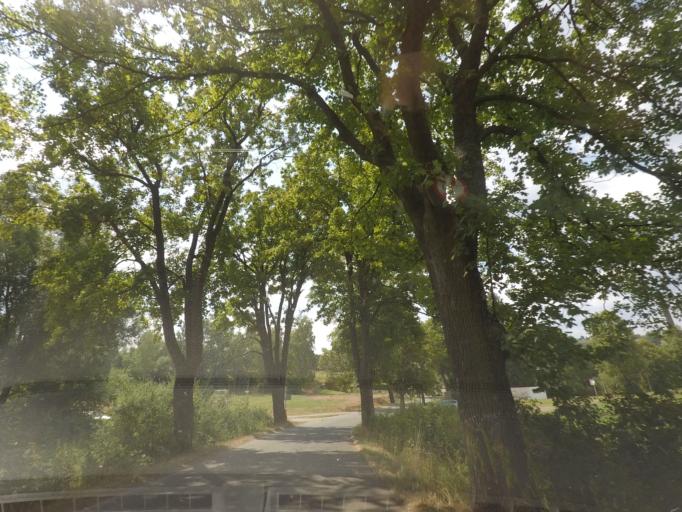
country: CZ
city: Radvanice
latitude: 50.5971
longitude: 16.0437
